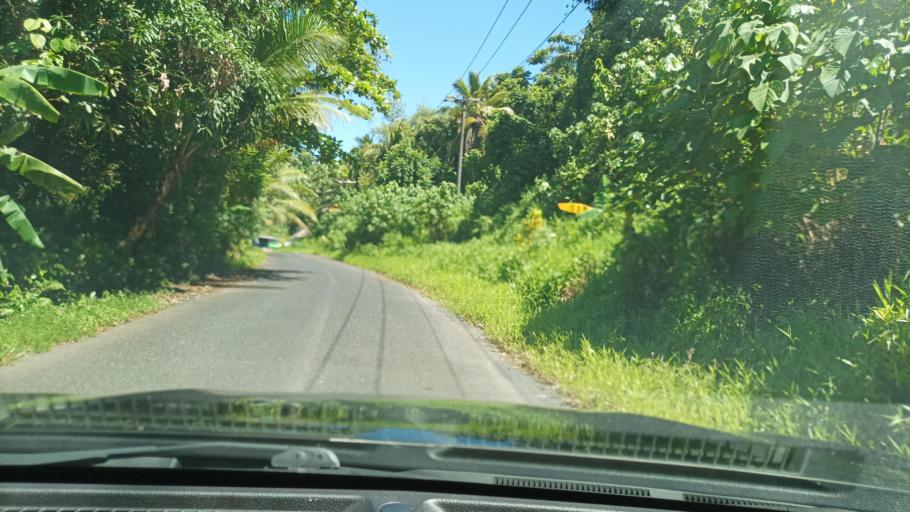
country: FM
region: Pohnpei
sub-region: Madolenihm Municipality
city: Madolenihm Municipality Government
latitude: 6.8477
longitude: 158.3010
